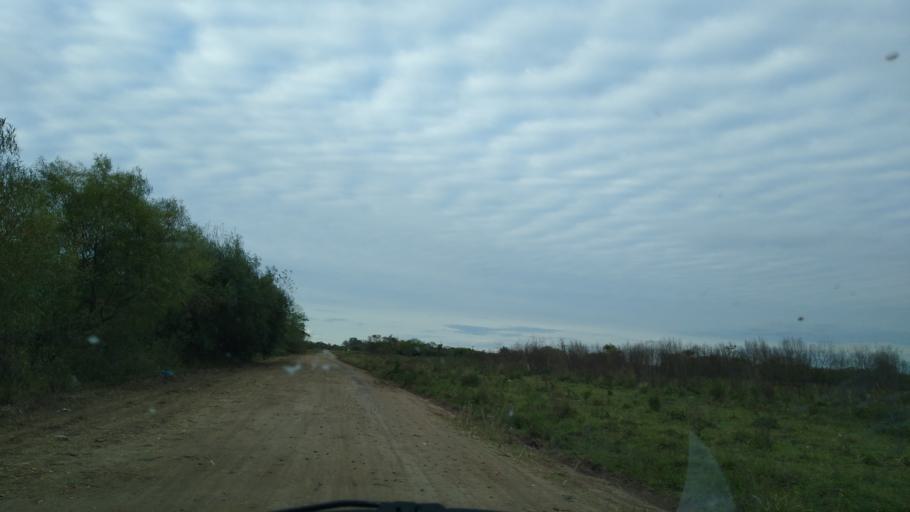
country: AR
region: Chaco
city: Puerto Tirol
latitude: -27.3911
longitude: -59.0505
